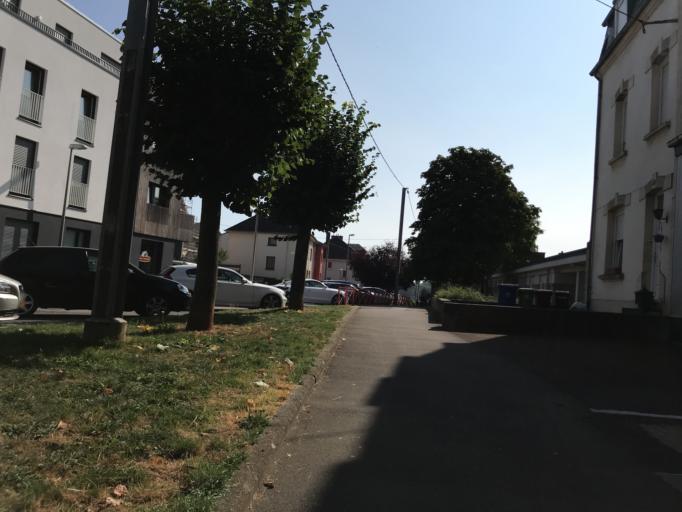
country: LU
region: Luxembourg
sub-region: Canton d'Esch-sur-Alzette
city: Niedercorn
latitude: 49.5372
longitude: 5.8914
